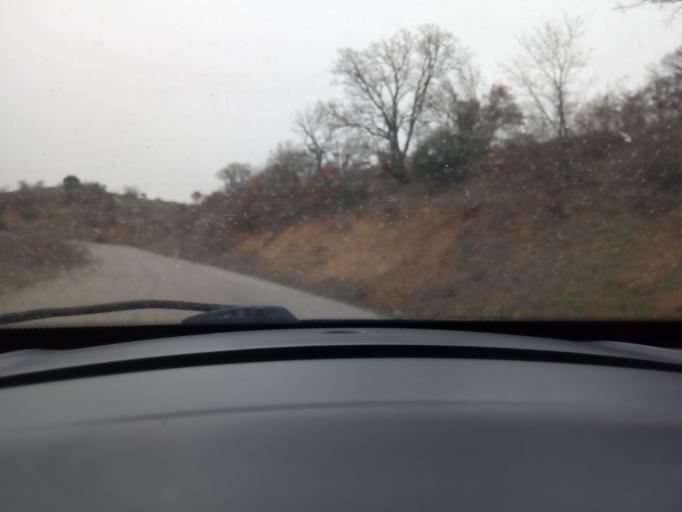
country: TR
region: Balikesir
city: Susurluk
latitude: 39.9099
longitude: 28.1060
